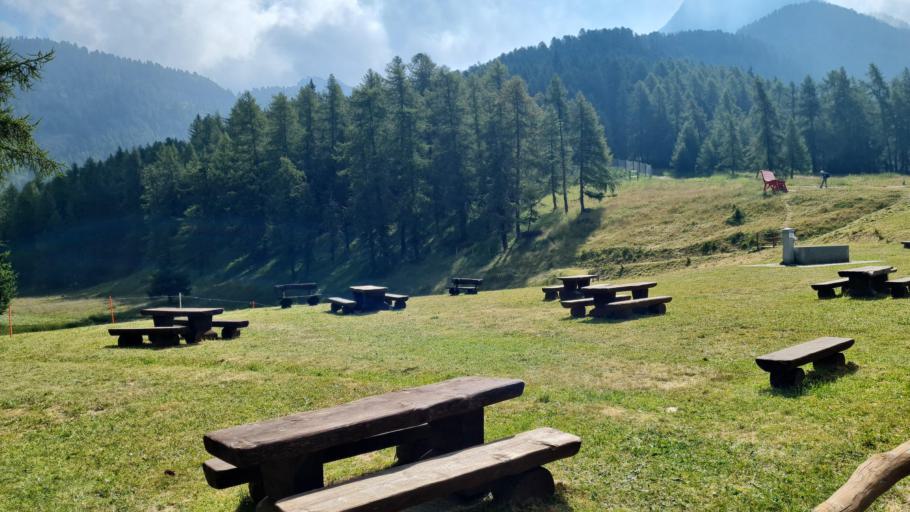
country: IT
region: Aosta Valley
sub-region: Valle d'Aosta
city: La Magdeleine
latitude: 45.8219
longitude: 7.6186
